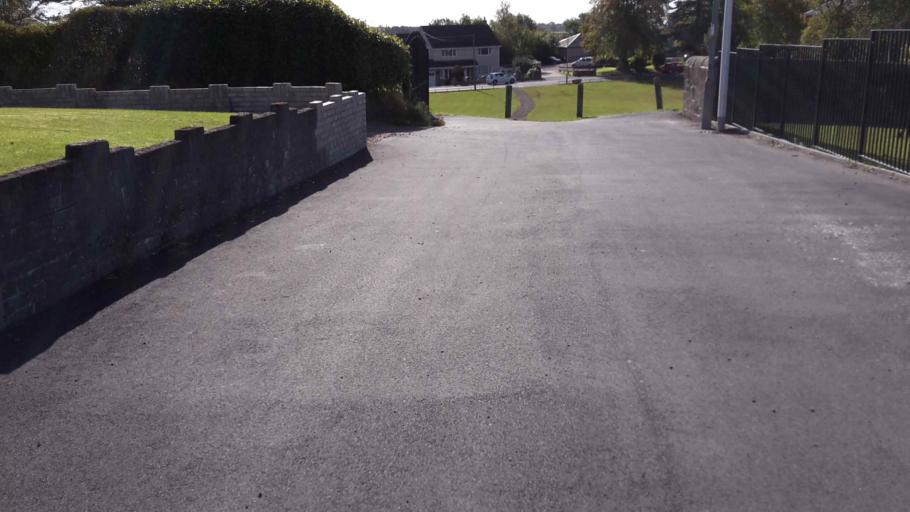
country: GB
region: Scotland
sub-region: South Lanarkshire
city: Carluke
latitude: 55.7339
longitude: -3.8415
